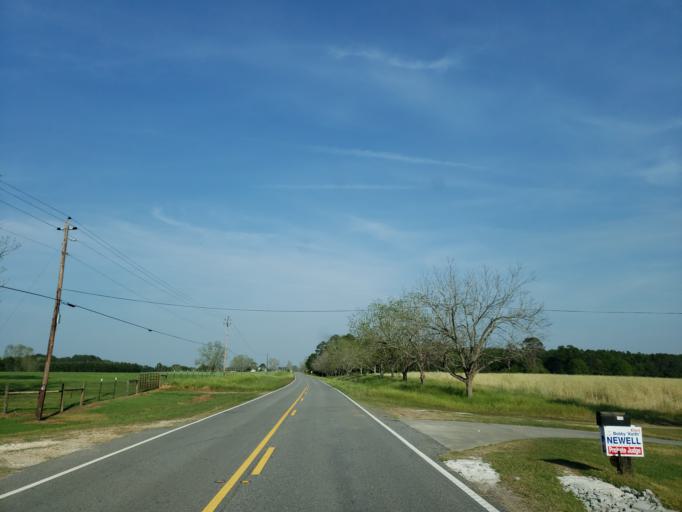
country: US
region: Georgia
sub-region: Tift County
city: Tifton
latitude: 31.5704
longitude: -83.5439
